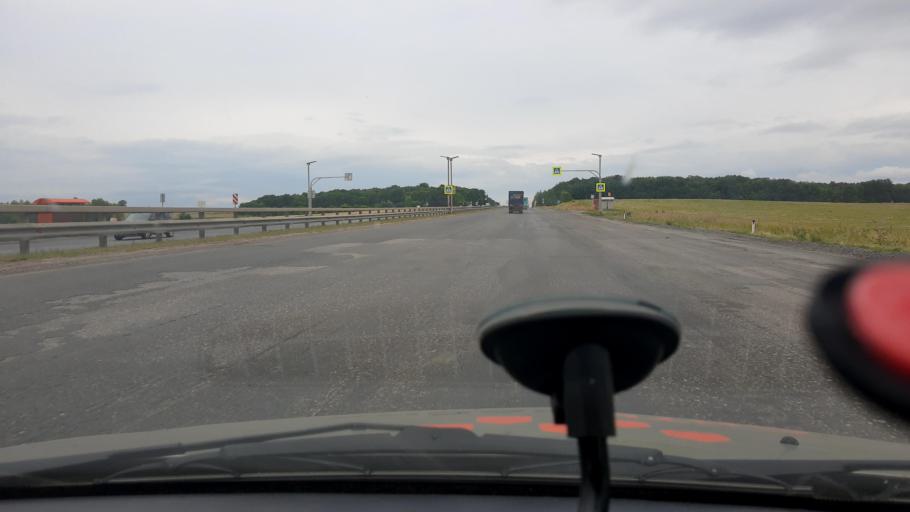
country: RU
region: Bashkortostan
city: Avdon
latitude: 54.6514
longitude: 55.6663
